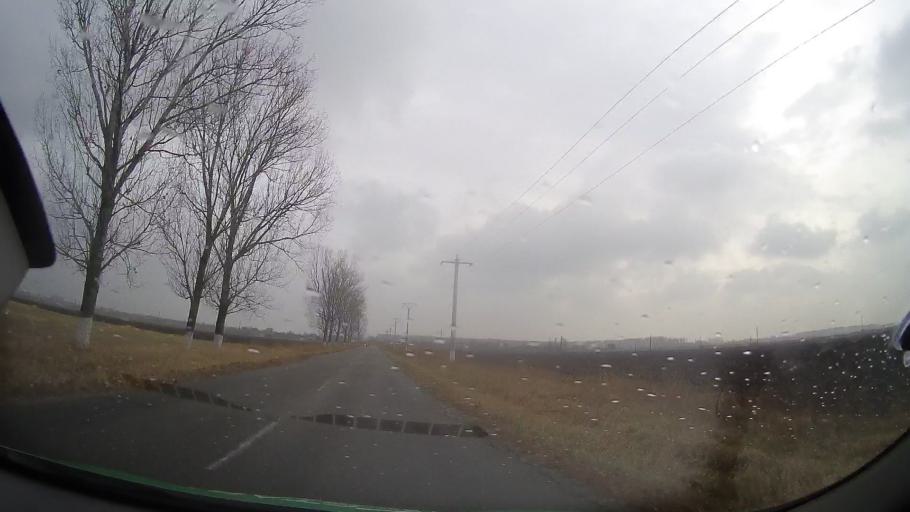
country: RO
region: Prahova
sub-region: Comuna Draganesti
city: Draganesti
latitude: 44.8327
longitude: 26.2731
